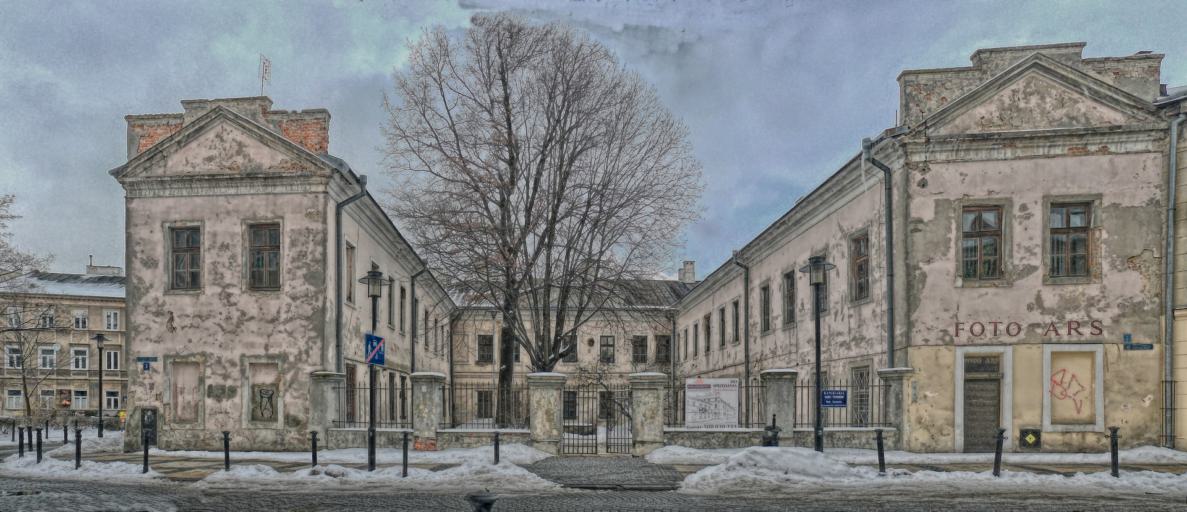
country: PL
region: Lublin Voivodeship
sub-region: Powiat lubelski
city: Lublin
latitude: 51.2487
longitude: 22.5623
